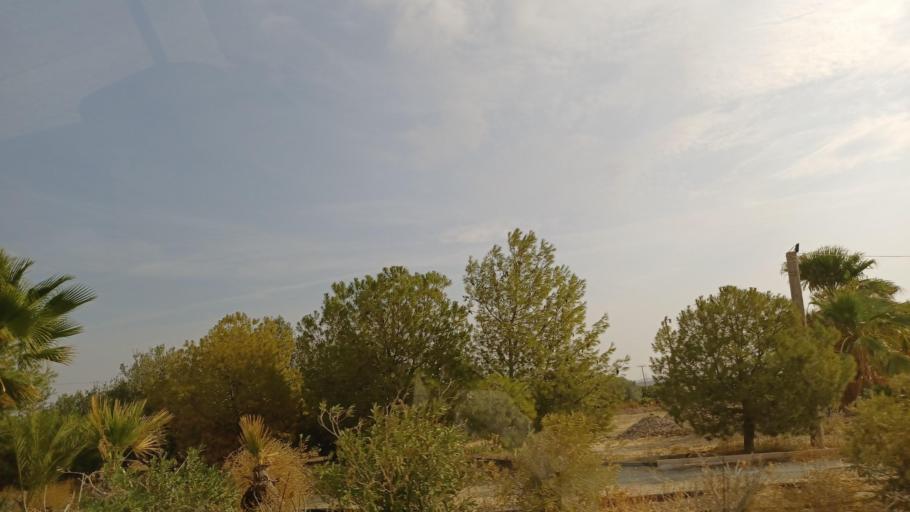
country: CY
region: Larnaka
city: Aradippou
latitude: 34.9995
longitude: 33.5745
